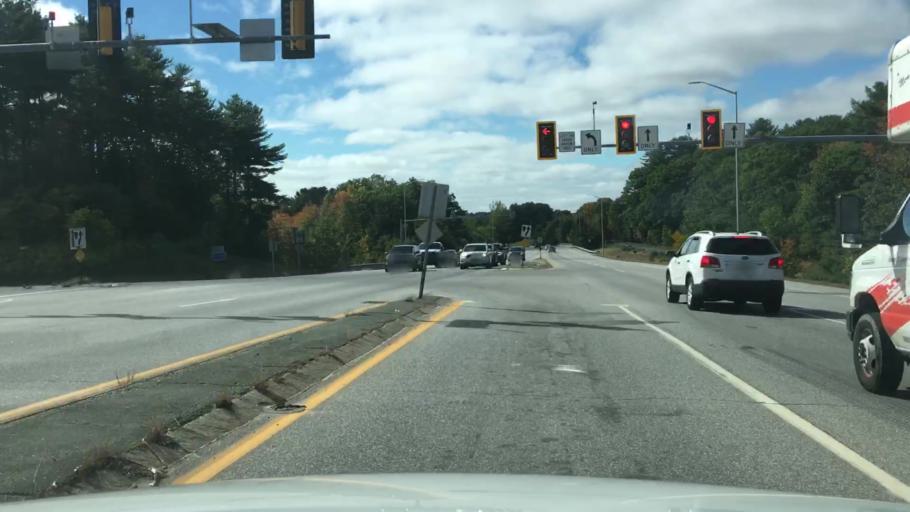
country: US
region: Maine
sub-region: Cumberland County
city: Brunswick
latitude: 43.9284
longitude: -69.9496
